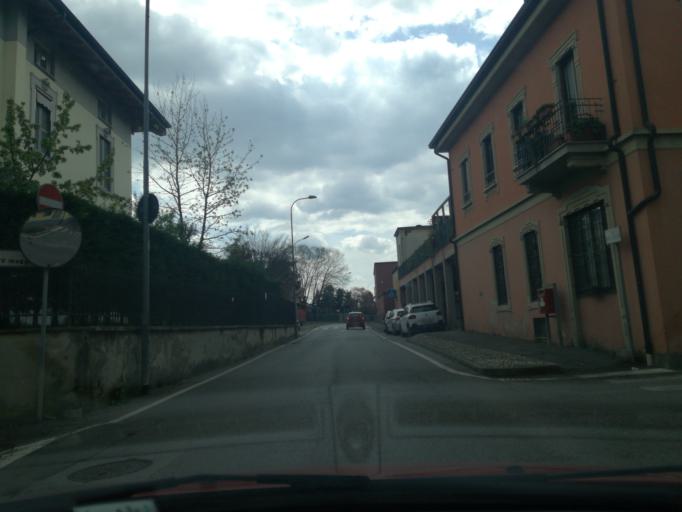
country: IT
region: Lombardy
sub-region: Provincia di Monza e Brianza
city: Lesmo
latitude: 45.6309
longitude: 9.3034
